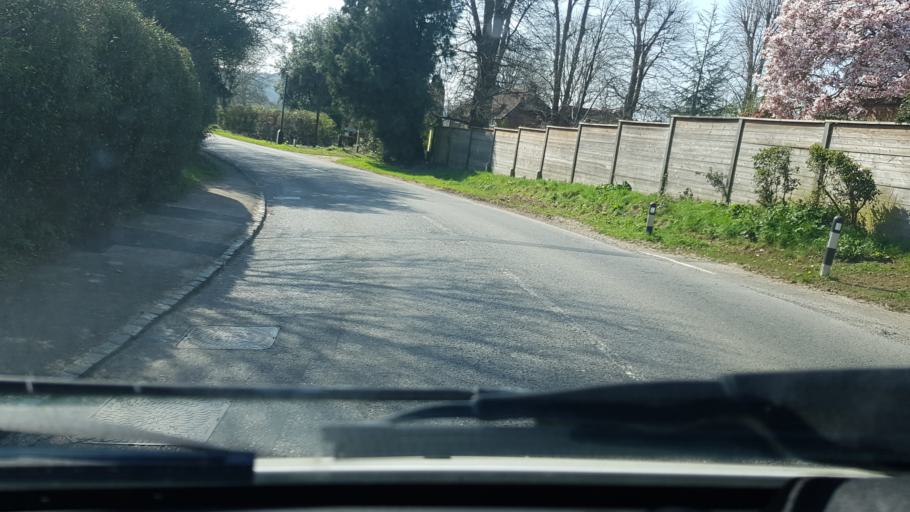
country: GB
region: England
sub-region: West Sussex
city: Fernhurst
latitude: 51.0449
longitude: -0.7250
